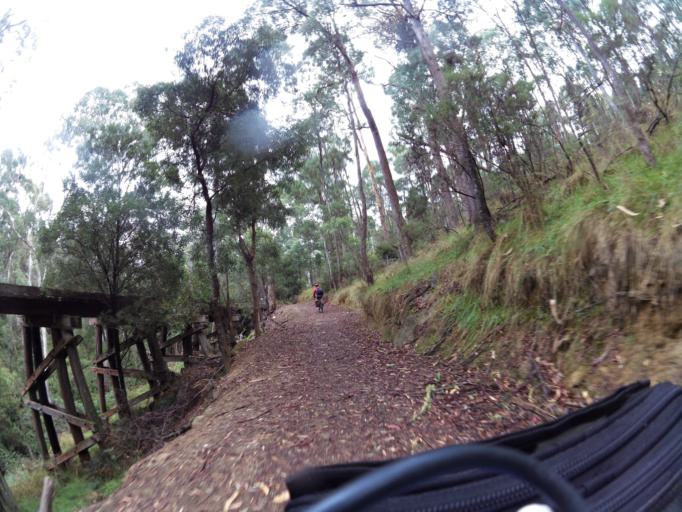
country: AU
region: New South Wales
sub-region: Greater Hume Shire
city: Holbrook
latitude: -36.1649
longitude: 147.4852
